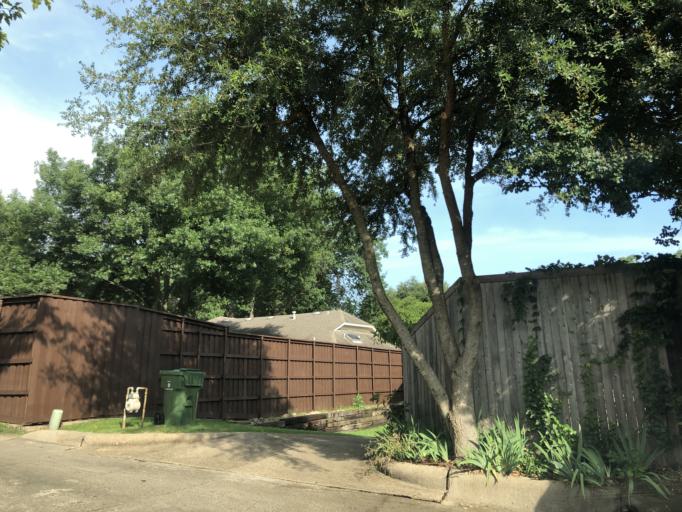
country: US
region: Texas
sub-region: Dallas County
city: Sunnyvale
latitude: 32.8462
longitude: -96.6106
